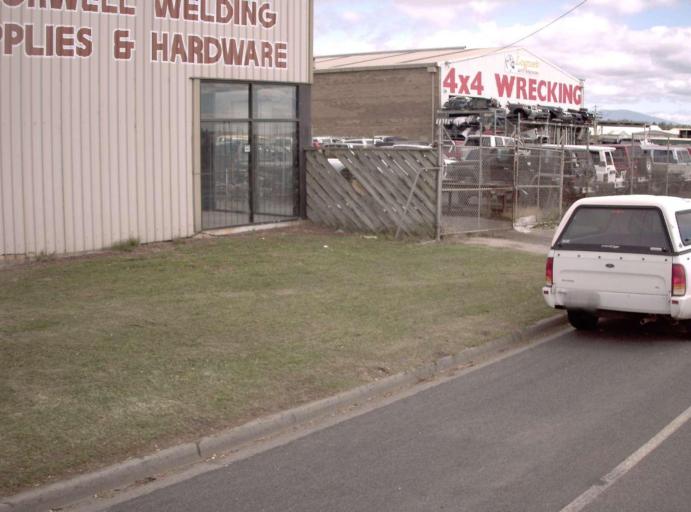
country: AU
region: Victoria
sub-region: Latrobe
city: Morwell
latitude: -38.2257
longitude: 146.4425
